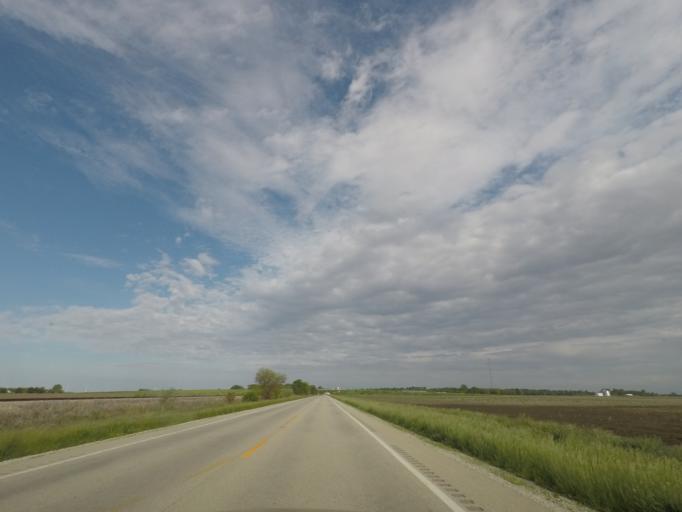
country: US
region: Illinois
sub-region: Logan County
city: Mount Pulaski
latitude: 39.9983
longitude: -89.2653
